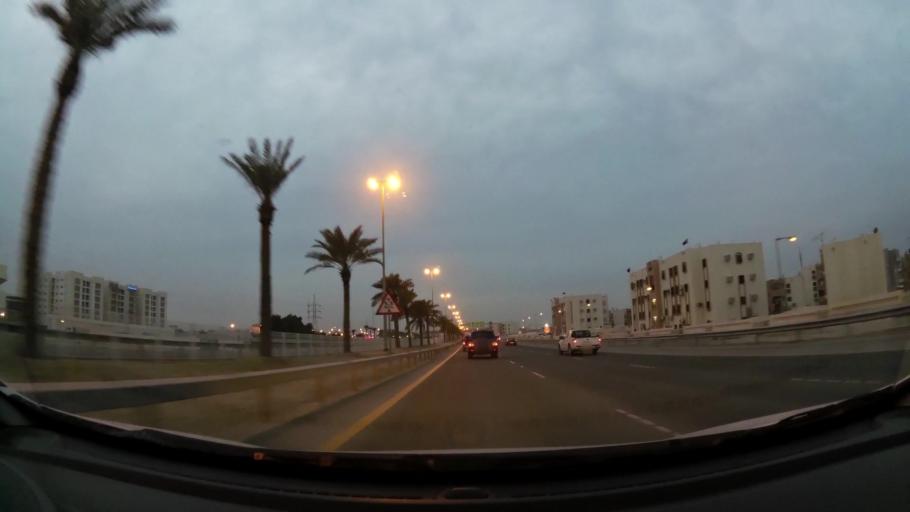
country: BH
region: Northern
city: Madinat `Isa
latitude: 26.1565
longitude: 50.5683
